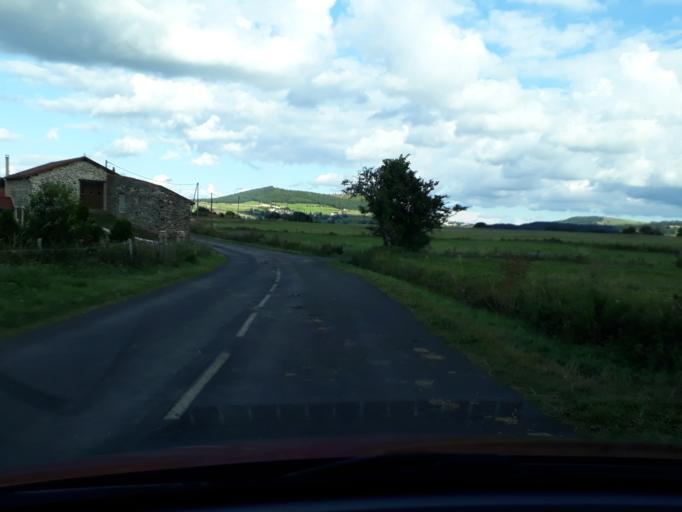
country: FR
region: Languedoc-Roussillon
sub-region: Departement de la Lozere
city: Langogne
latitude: 44.8229
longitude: 3.9226
